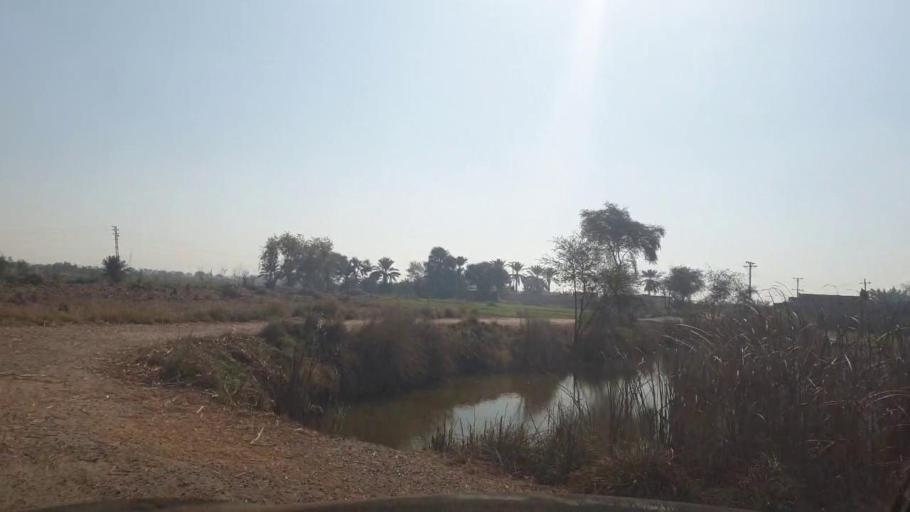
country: PK
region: Sindh
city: Ghotki
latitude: 27.9841
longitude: 69.3558
